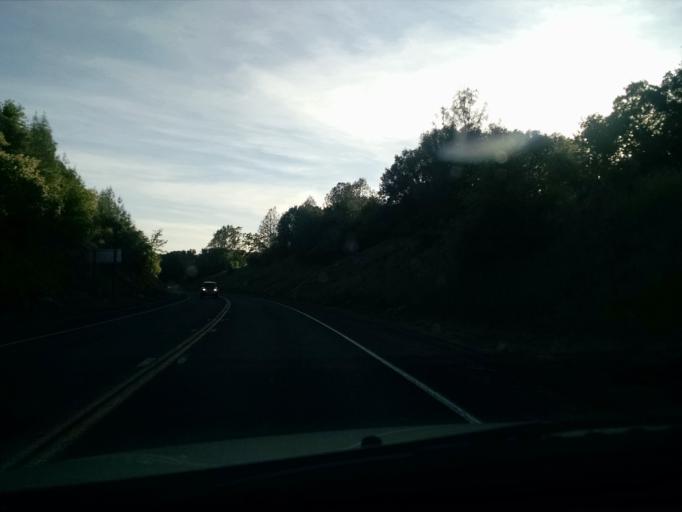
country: US
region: California
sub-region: Mariposa County
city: Mariposa
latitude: 37.4627
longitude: -119.8973
